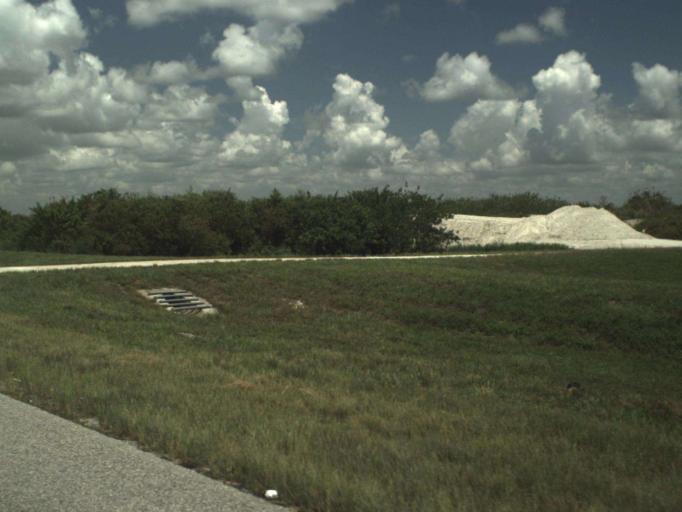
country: US
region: Florida
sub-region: Indian River County
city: Fellsmere
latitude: 27.6407
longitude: -80.6785
